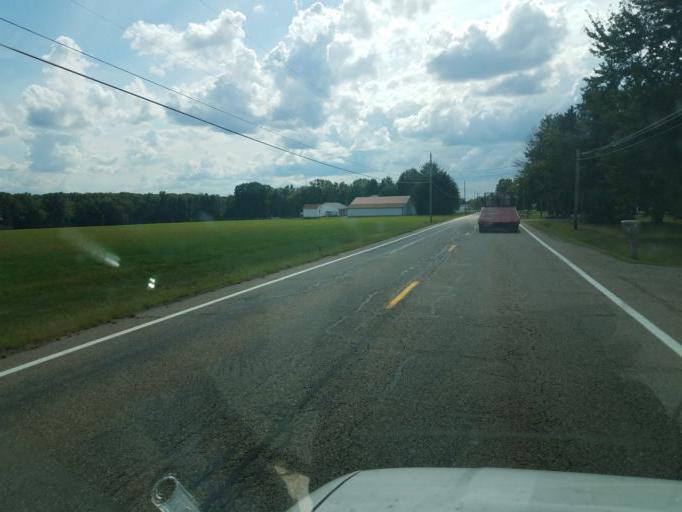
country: US
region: Ohio
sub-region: Portage County
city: Ravenna
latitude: 41.2035
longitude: -81.1907
